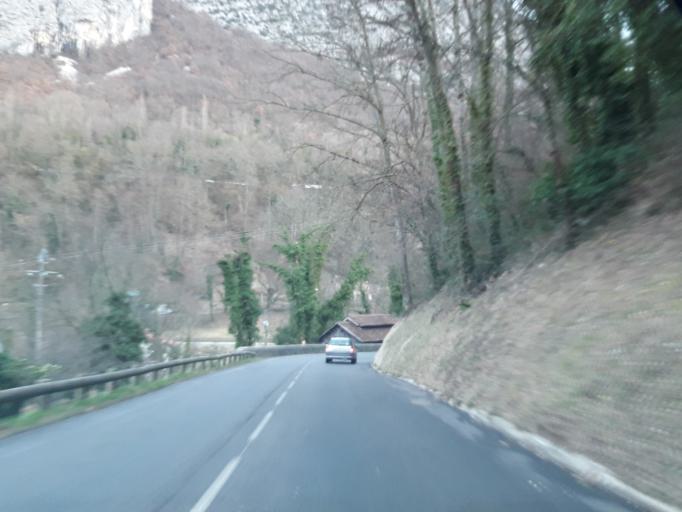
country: FR
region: Rhone-Alpes
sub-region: Departement de l'Isere
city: Pont-en-Royans
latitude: 45.0567
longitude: 5.3415
